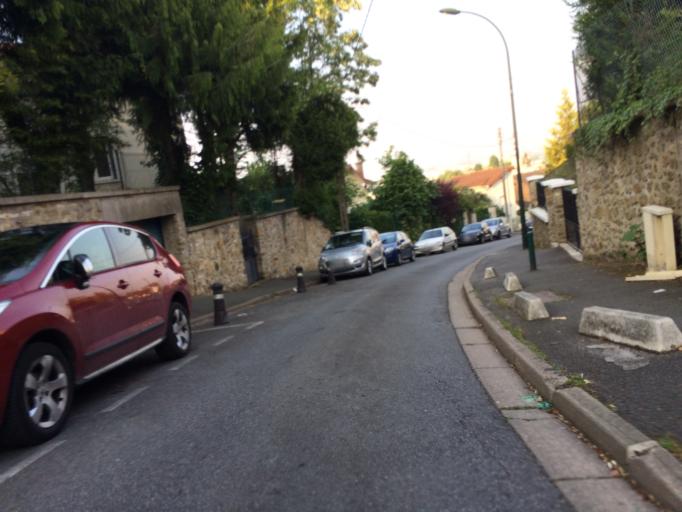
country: FR
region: Ile-de-France
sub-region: Departement de l'Essonne
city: Palaiseau
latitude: 48.7207
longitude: 2.2418
